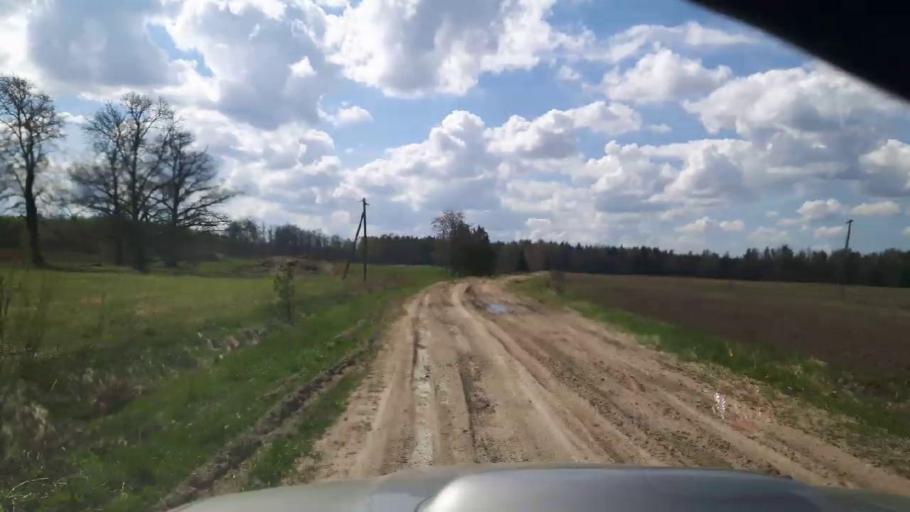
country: EE
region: Paernumaa
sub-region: Vaendra vald (alev)
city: Vandra
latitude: 58.5405
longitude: 25.0691
